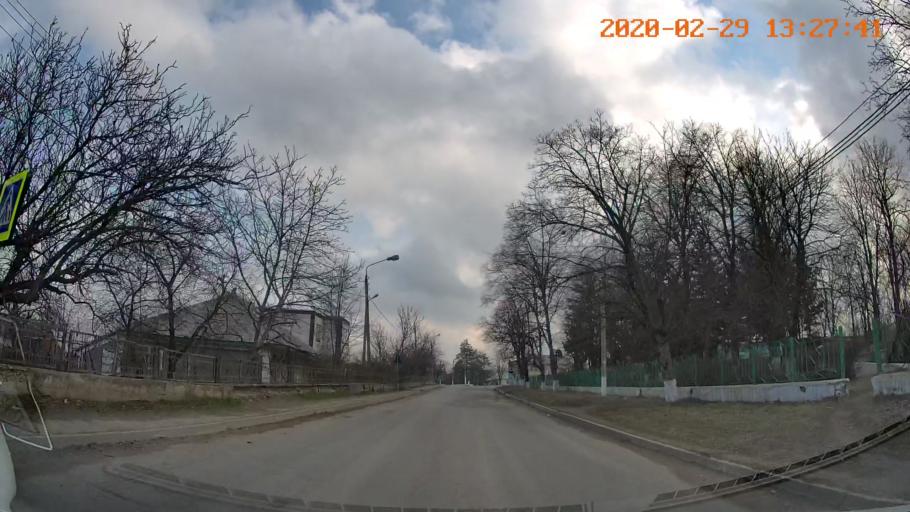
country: MD
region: Telenesti
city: Camenca
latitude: 47.9107
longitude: 28.6441
